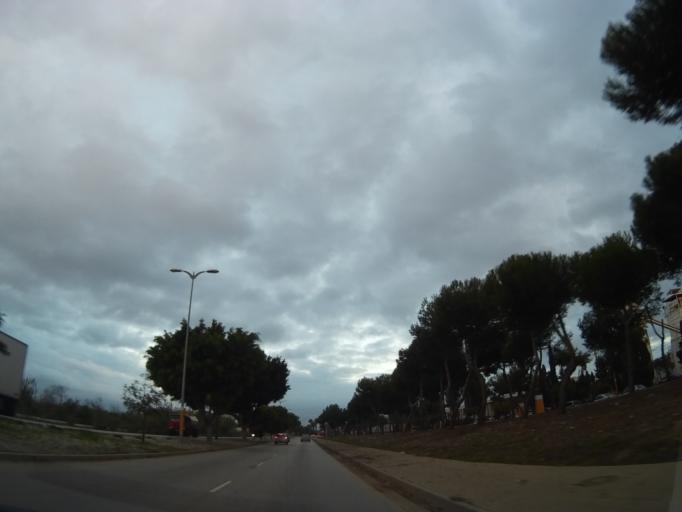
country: ES
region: Andalusia
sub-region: Provincia de Malaga
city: Malaga
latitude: 36.6884
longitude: -4.4797
